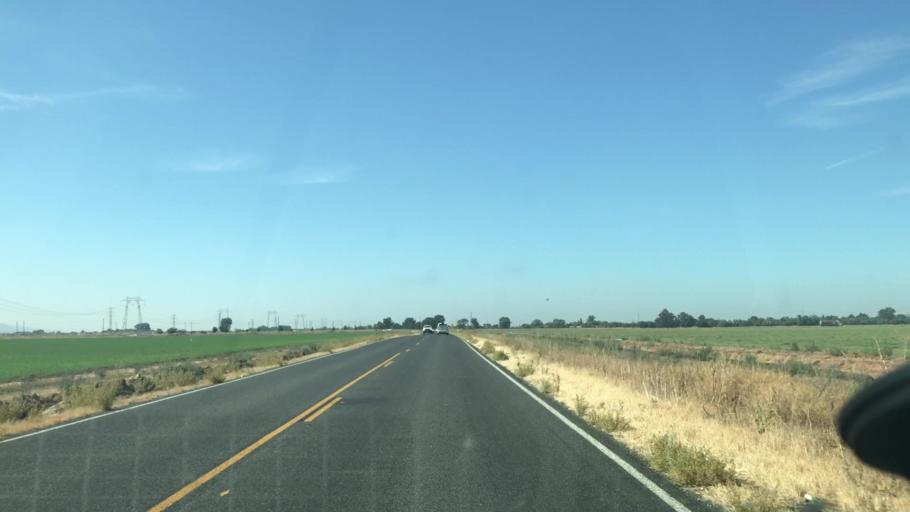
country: US
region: California
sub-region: Solano County
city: Vacaville
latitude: 38.3331
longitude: -121.9165
